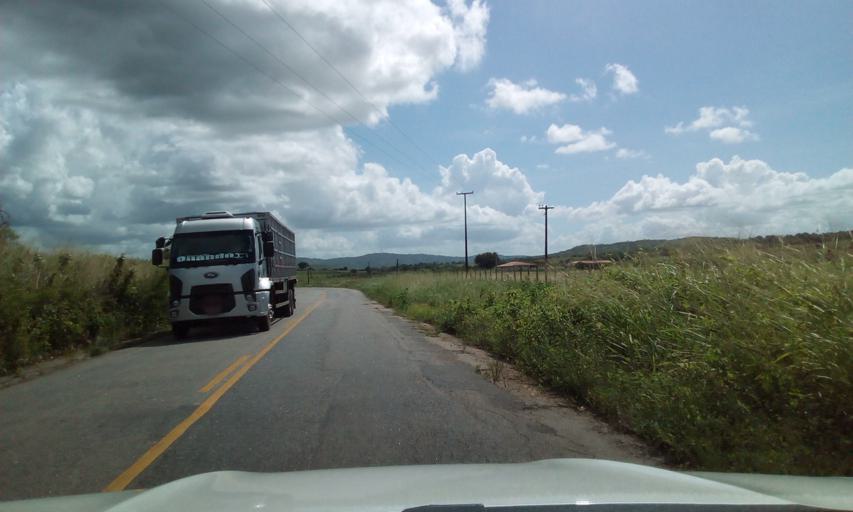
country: BR
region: Paraiba
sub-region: Guarabira
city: Guarabira
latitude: -6.8590
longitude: -35.4250
